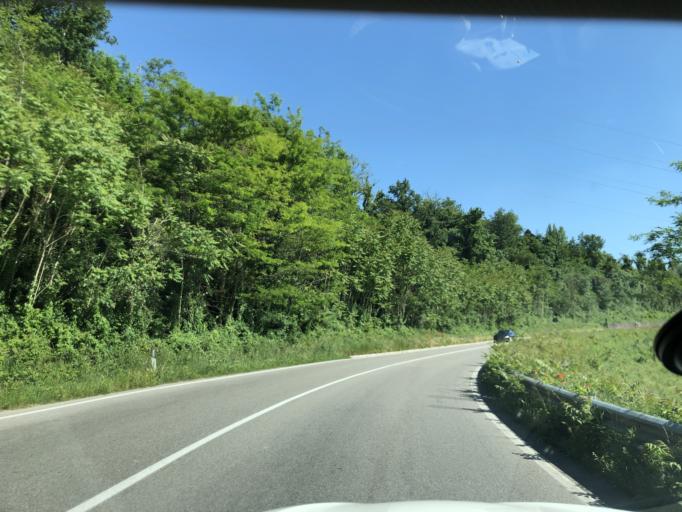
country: IT
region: Lombardy
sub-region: Citta metropolitana di Milano
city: Nosate
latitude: 45.5863
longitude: 8.7073
